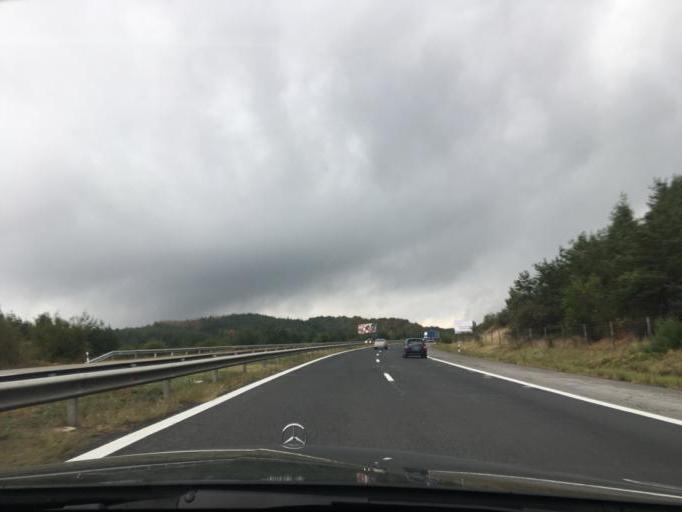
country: BG
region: Sofiya
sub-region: Obshtina Elin Pelin
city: Elin Pelin
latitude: 42.5804
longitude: 23.6529
